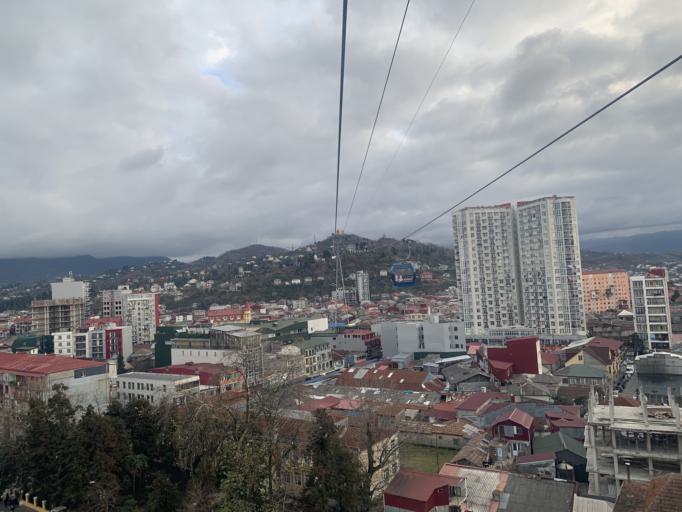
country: GE
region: Ajaria
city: Batumi
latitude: 41.6455
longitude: 41.6464
